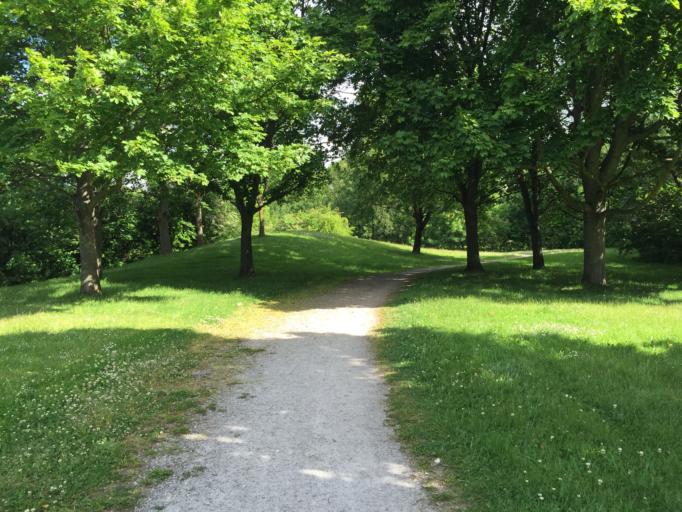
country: SE
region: Skane
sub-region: Lunds Kommun
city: Lund
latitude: 55.7368
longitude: 13.1800
